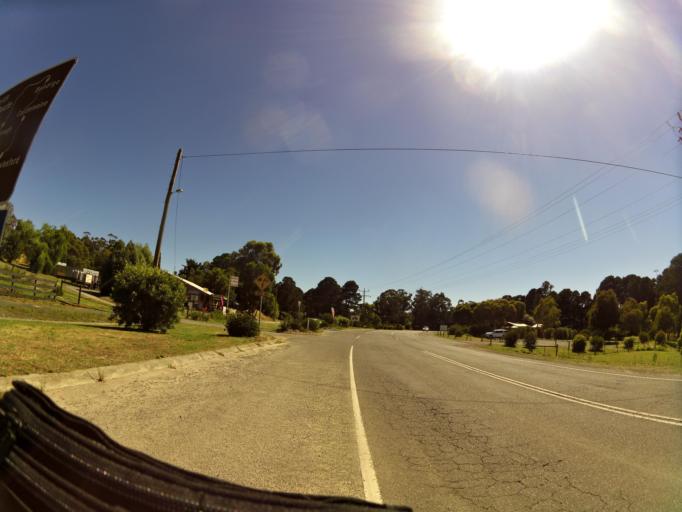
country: AU
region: Victoria
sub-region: Ballarat North
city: Delacombe
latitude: -37.6834
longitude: 143.5650
